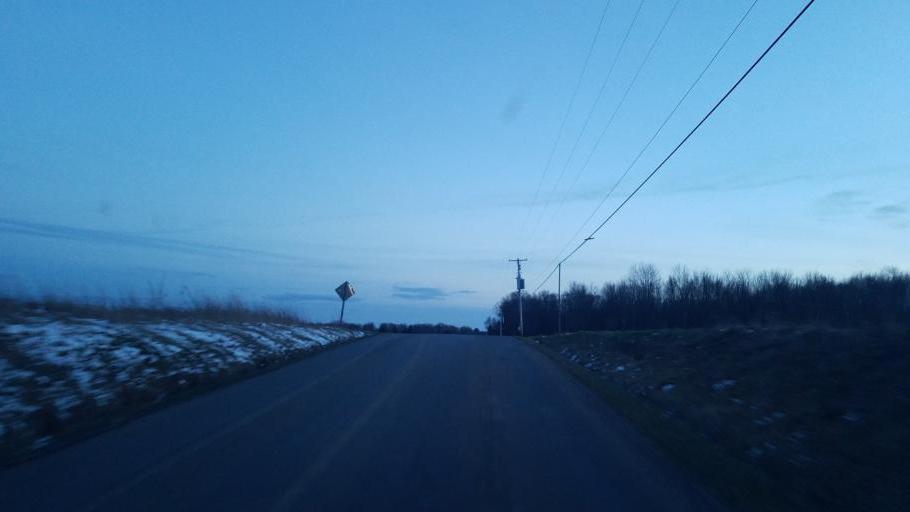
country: US
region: Ohio
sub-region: Ashland County
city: Ashland
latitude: 40.8398
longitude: -82.2795
